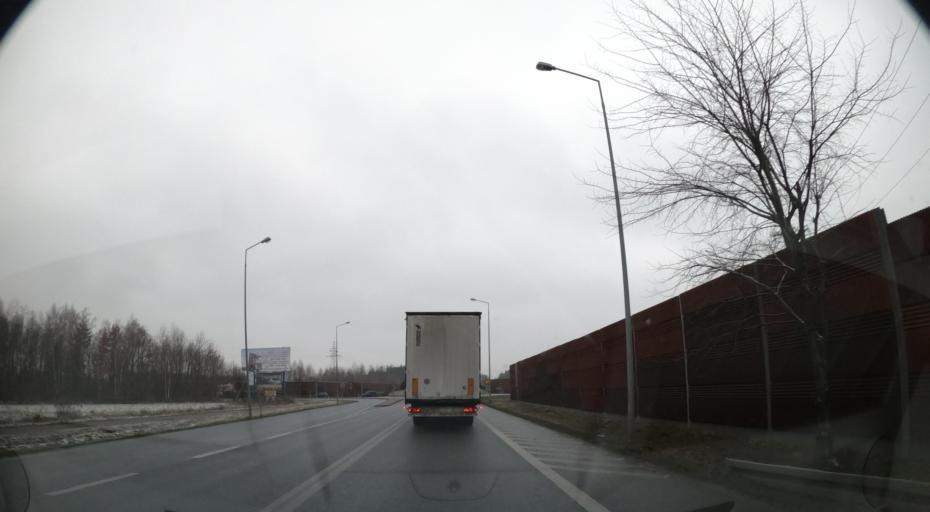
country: PL
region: Masovian Voivodeship
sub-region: Powiat sochaczewski
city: Sochaczew
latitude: 52.2186
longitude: 20.2052
